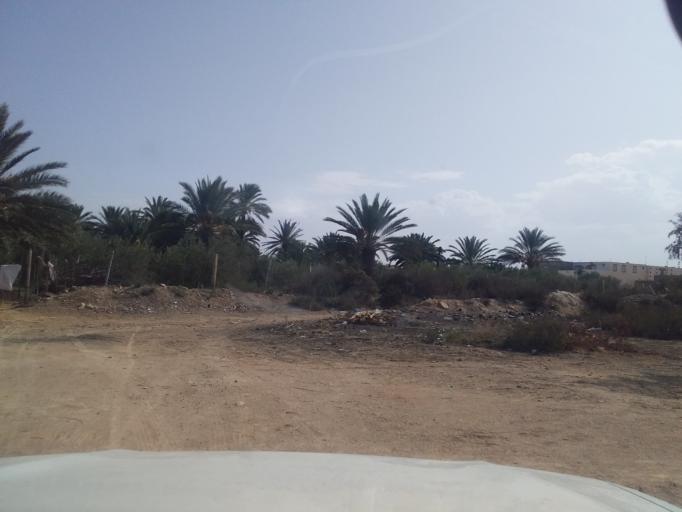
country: TN
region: Qabis
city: Gabes
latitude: 33.6330
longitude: 10.2869
